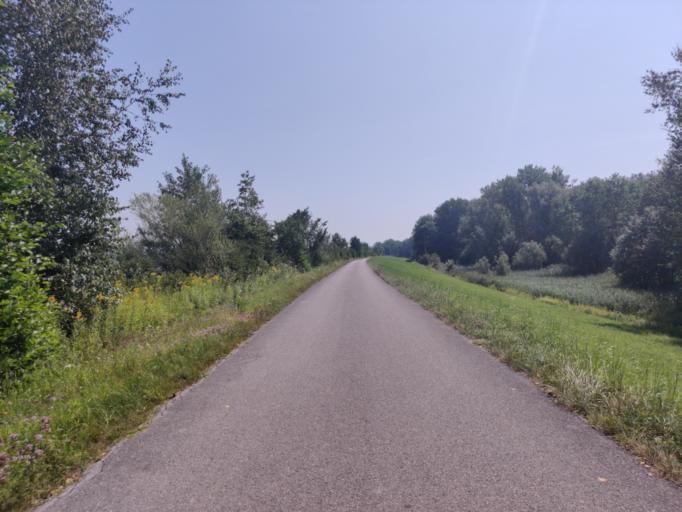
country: AT
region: Upper Austria
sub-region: Politischer Bezirk Urfahr-Umgebung
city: Goldworth
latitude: 48.3124
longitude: 14.0991
